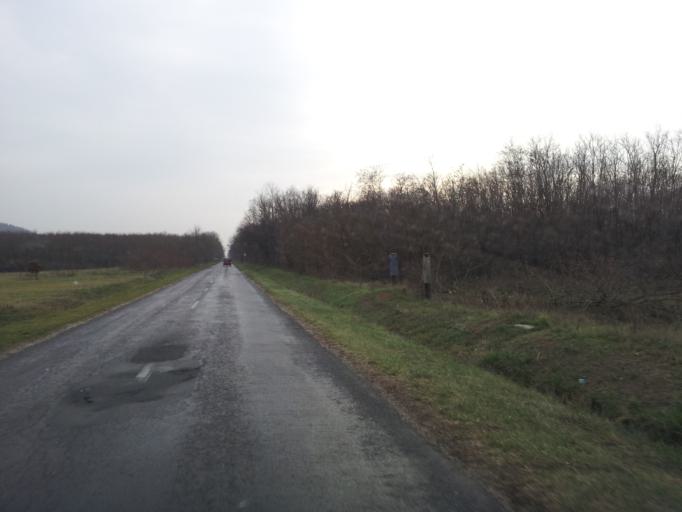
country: HU
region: Zala
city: Cserszegtomaj
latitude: 46.8537
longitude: 17.1985
